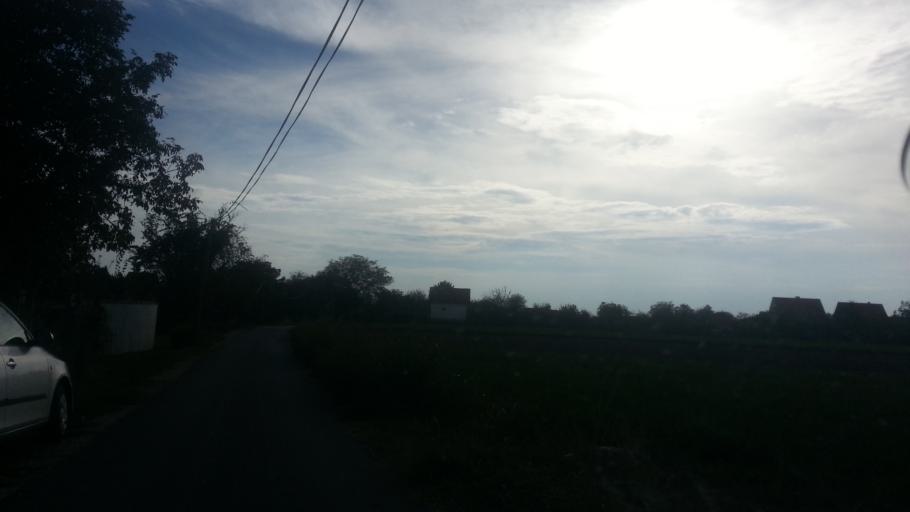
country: RS
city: Belegis
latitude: 45.0246
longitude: 20.3508
